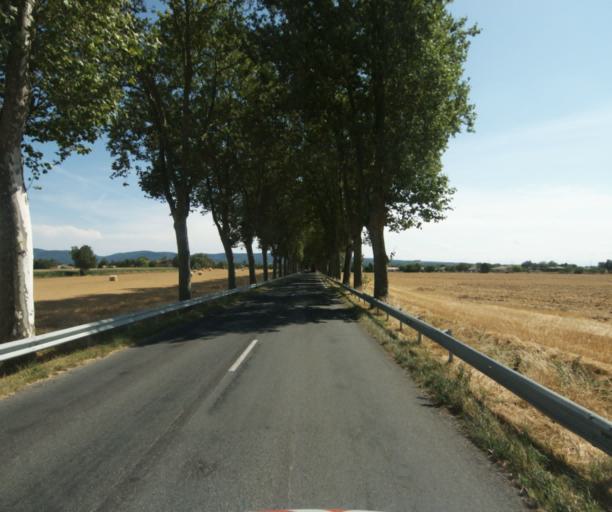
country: FR
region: Midi-Pyrenees
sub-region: Departement de la Haute-Garonne
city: Revel
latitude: 43.4940
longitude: 2.0128
